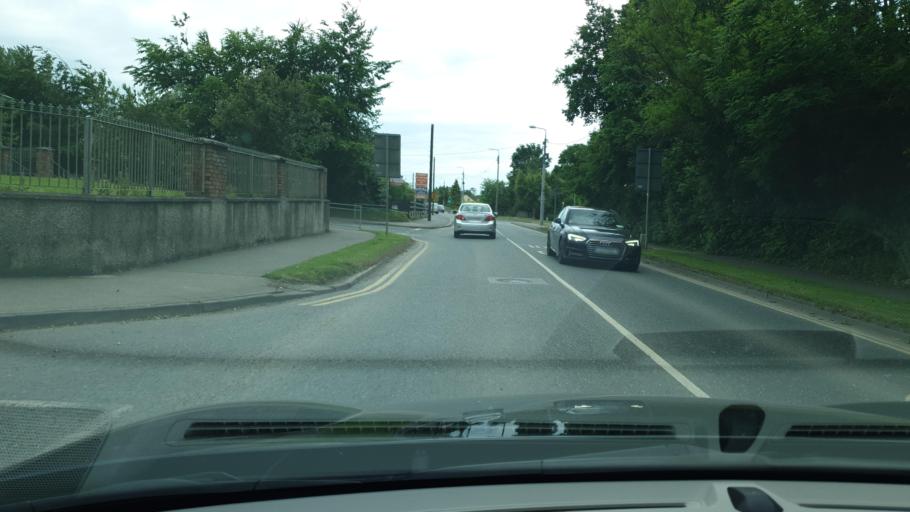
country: IE
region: Leinster
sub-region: An Mhi
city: Ratoath
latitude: 53.5020
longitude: -6.4672
